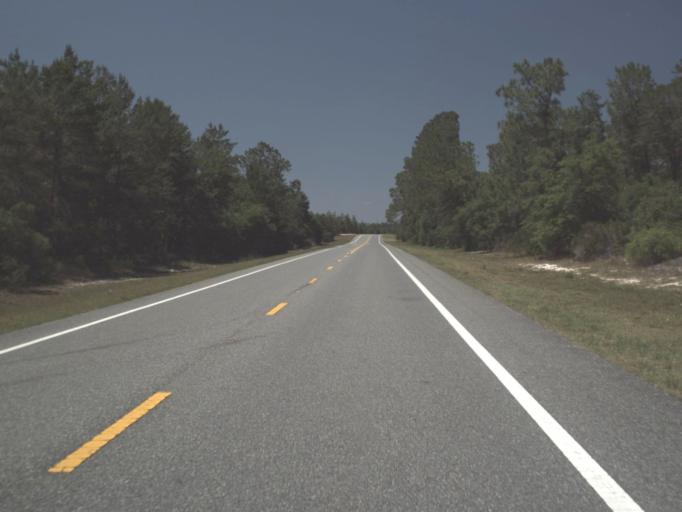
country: US
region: Florida
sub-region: Lake County
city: Astor
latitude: 29.1277
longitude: -81.6213
